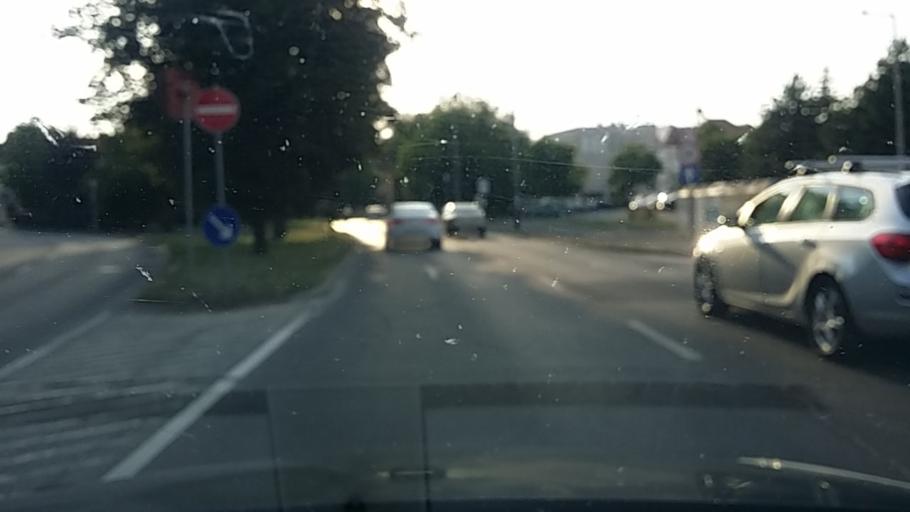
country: HU
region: Borsod-Abauj-Zemplen
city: Miskolc
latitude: 48.1022
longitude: 20.7784
